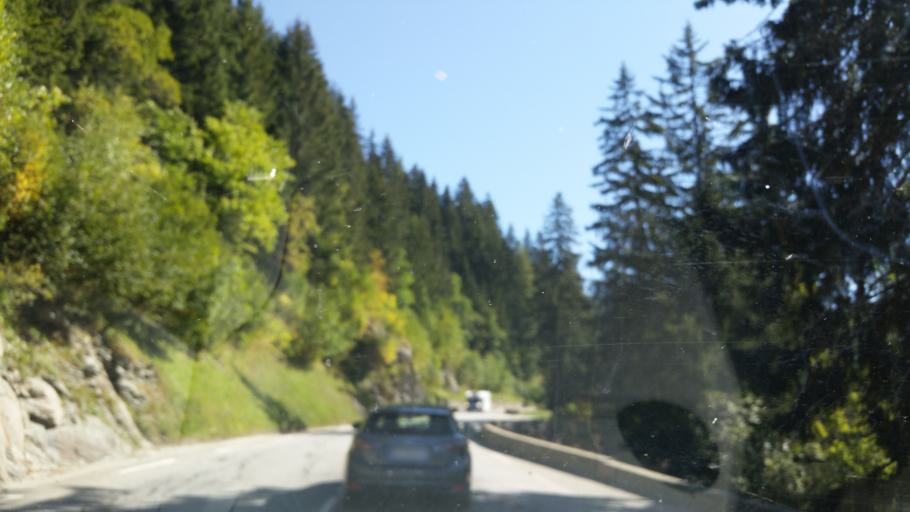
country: FR
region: Rhone-Alpes
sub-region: Departement de la Savoie
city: Tignes
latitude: 45.5401
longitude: 6.9109
